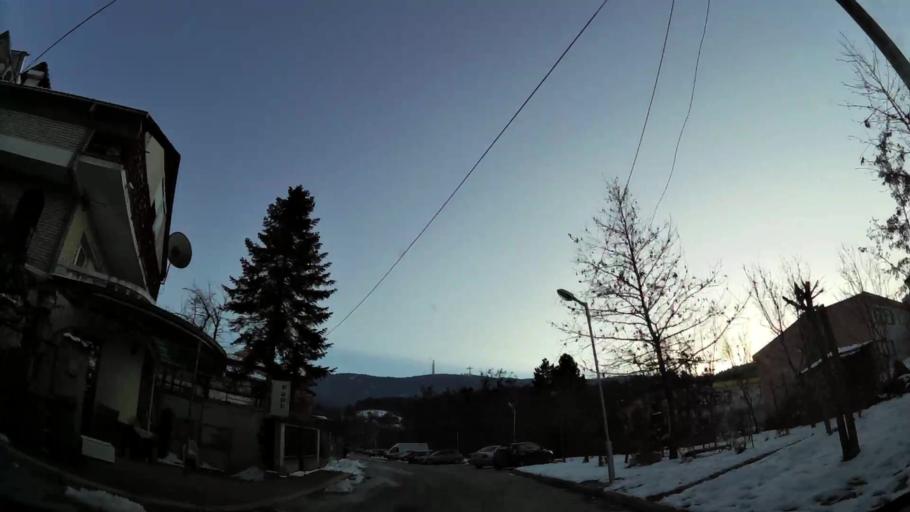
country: MK
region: Karpos
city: Skopje
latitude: 41.9902
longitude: 21.4060
